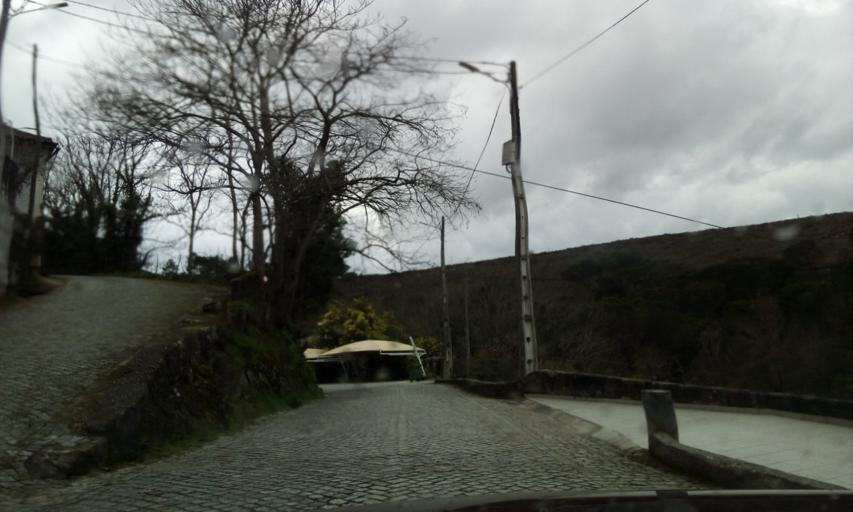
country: PT
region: Viseu
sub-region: Viseu
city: Rio de Loba
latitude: 40.6062
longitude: -7.8672
